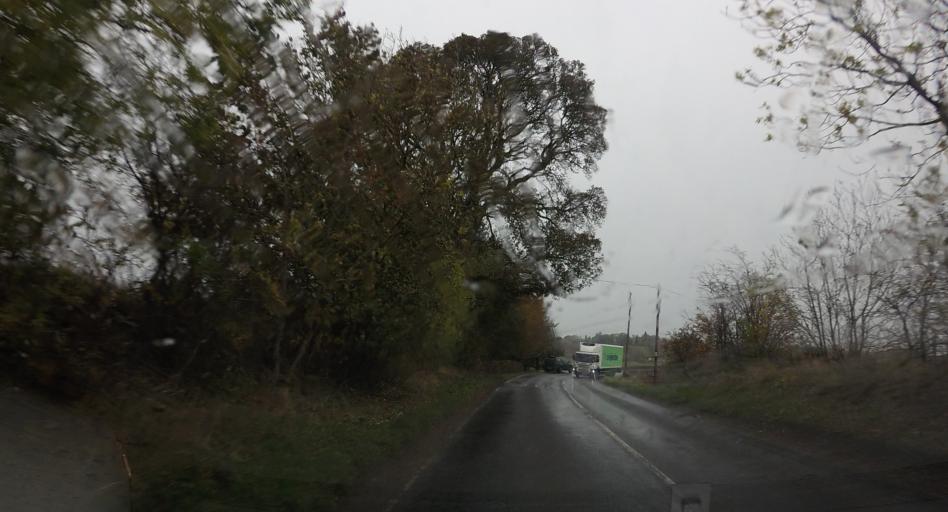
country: GB
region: Scotland
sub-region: Perth and Kinross
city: Coupar Angus
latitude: 56.5532
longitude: -3.2862
